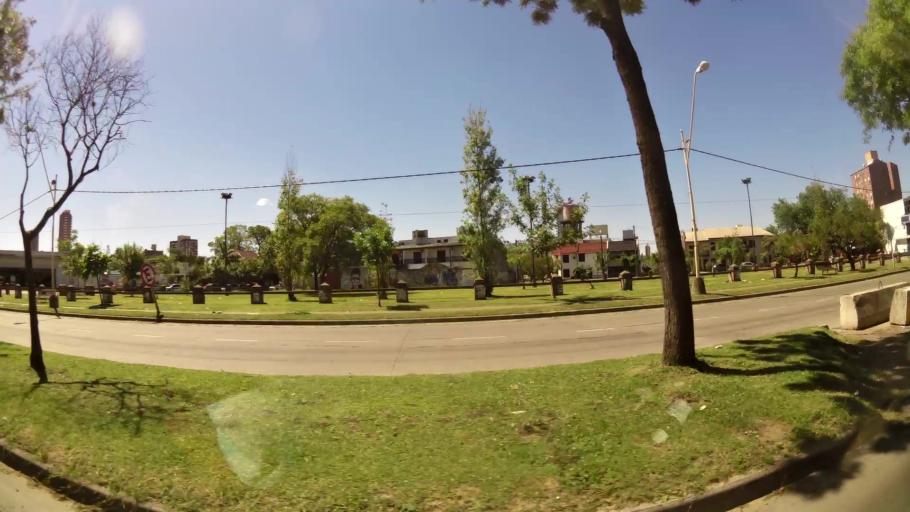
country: AR
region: Santa Fe
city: Santa Fe de la Vera Cruz
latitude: -31.6464
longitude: -60.6999
